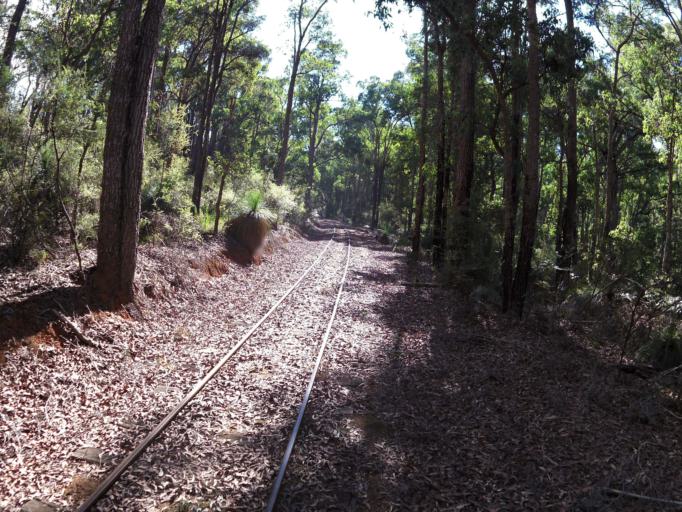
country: AU
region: Western Australia
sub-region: Waroona
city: Waroona
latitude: -32.7223
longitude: 116.1077
